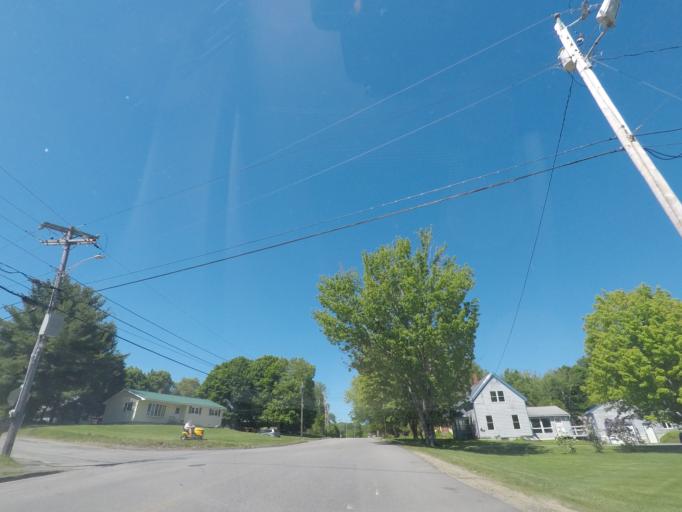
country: US
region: Maine
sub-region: Kennebec County
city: Gardiner
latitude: 44.2319
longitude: -69.7886
